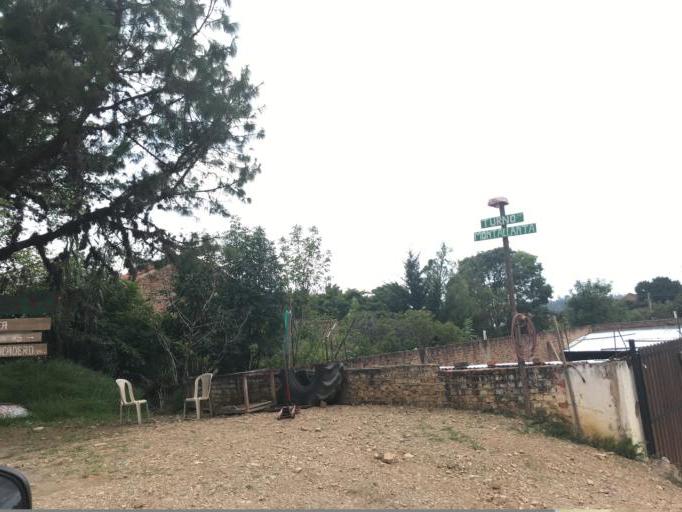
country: CO
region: Boyaca
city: Villa de Leiva
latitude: 5.6260
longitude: -73.5302
